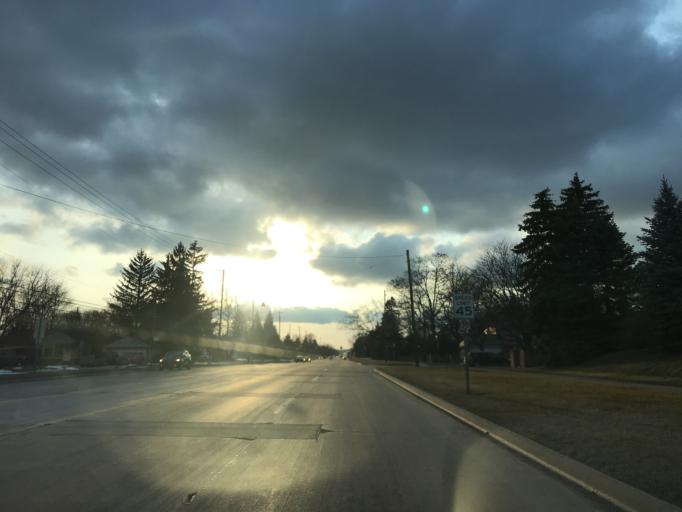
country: US
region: Michigan
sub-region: Oakland County
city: Farmington
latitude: 42.4261
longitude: -83.3814
